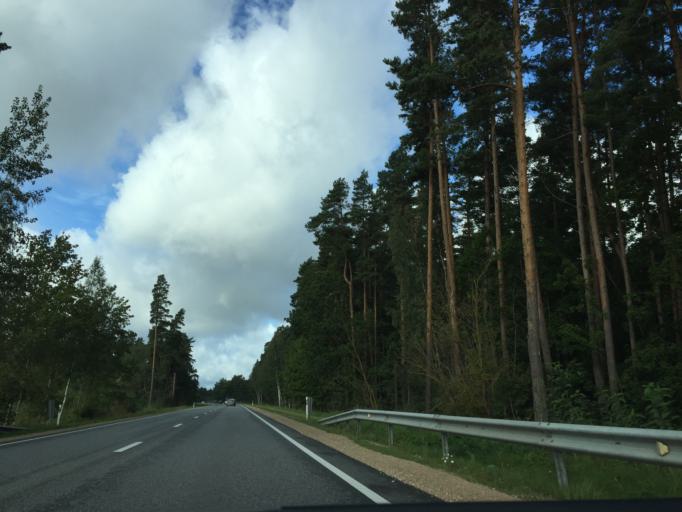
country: LV
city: Tireli
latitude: 56.9283
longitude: 23.6539
